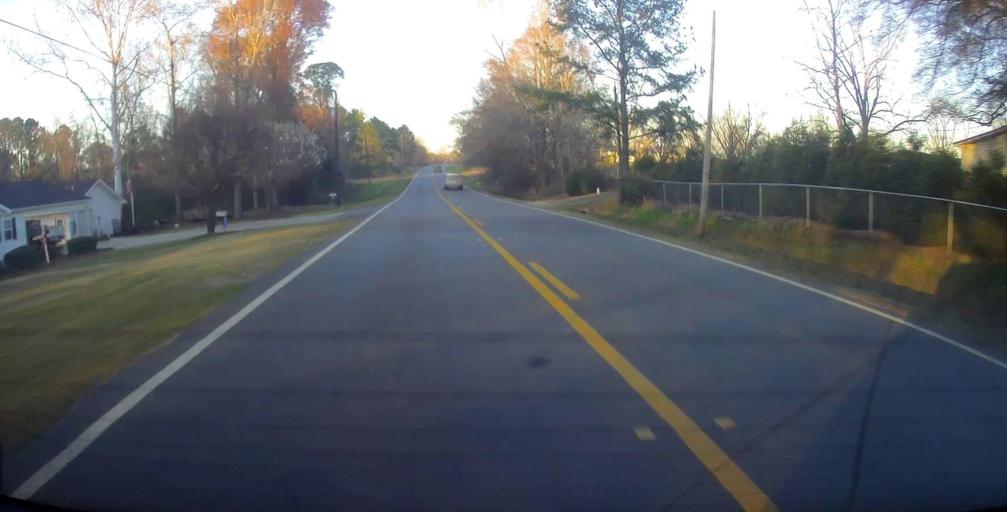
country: US
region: Georgia
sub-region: Dodge County
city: Chester
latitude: 32.3421
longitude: -83.0404
